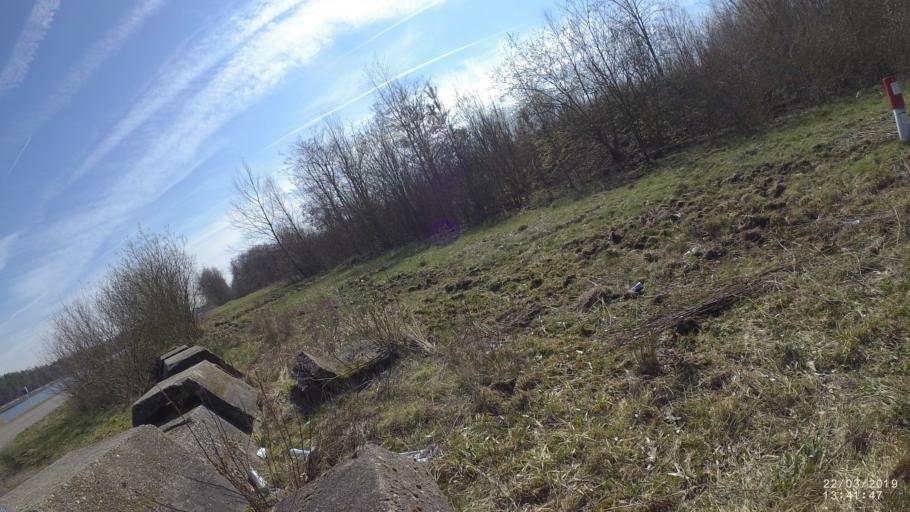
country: BE
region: Flanders
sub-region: Provincie Limburg
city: Zutendaal
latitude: 50.8990
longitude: 5.5655
